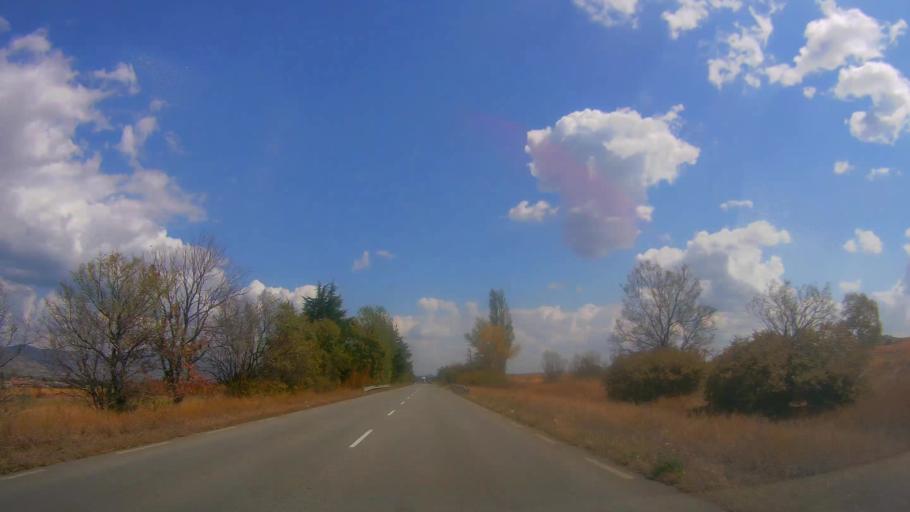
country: BG
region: Sliven
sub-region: Obshtina Tvurditsa
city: Tvurditsa
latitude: 42.6554
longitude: 25.9362
